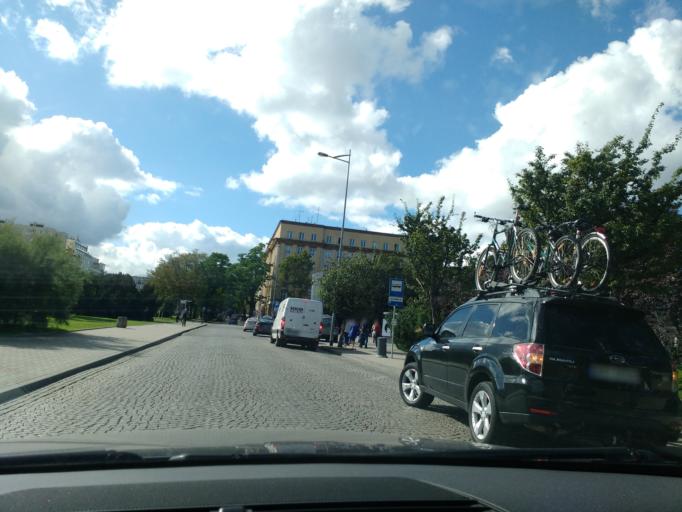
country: PL
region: Pomeranian Voivodeship
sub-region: Gdynia
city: Gdynia
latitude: 54.5193
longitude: 18.5485
